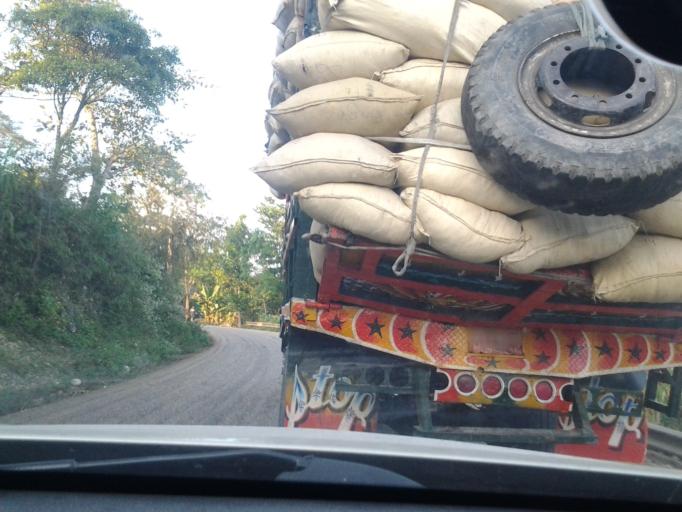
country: HT
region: Sud-Est
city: Jacmel
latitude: 18.3471
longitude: -72.5866
